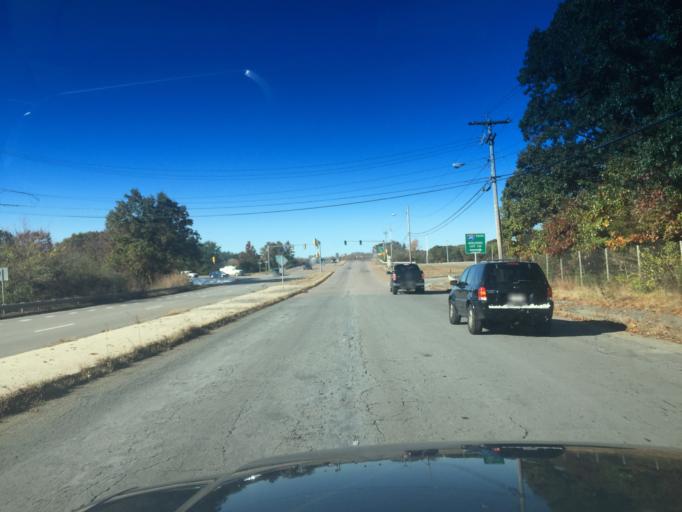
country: US
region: Massachusetts
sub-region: Bristol County
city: Raynham
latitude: 41.9604
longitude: -71.1212
